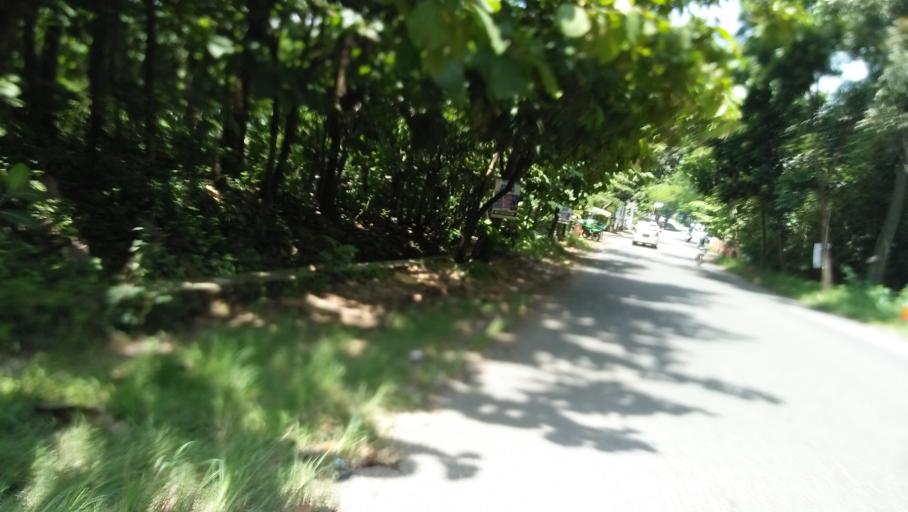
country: ID
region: Central Java
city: Mranggen
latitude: -7.0387
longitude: 110.4647
